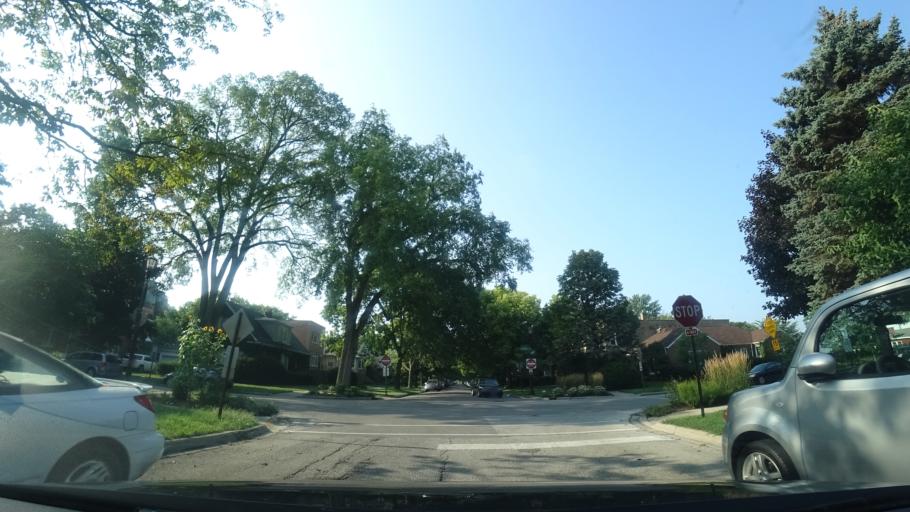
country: US
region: Illinois
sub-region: Cook County
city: Evanston
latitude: 42.0395
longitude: -87.6977
